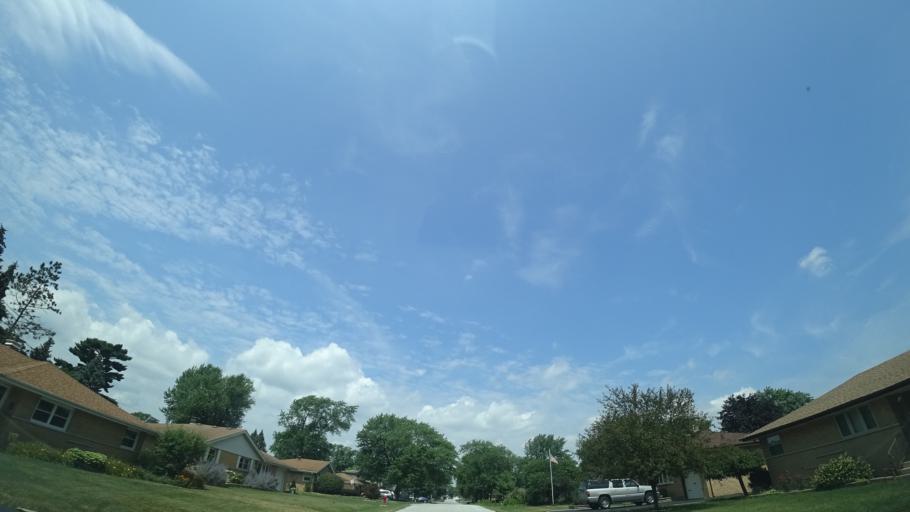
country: US
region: Illinois
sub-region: Cook County
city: Worth
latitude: 41.6832
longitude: -87.7822
